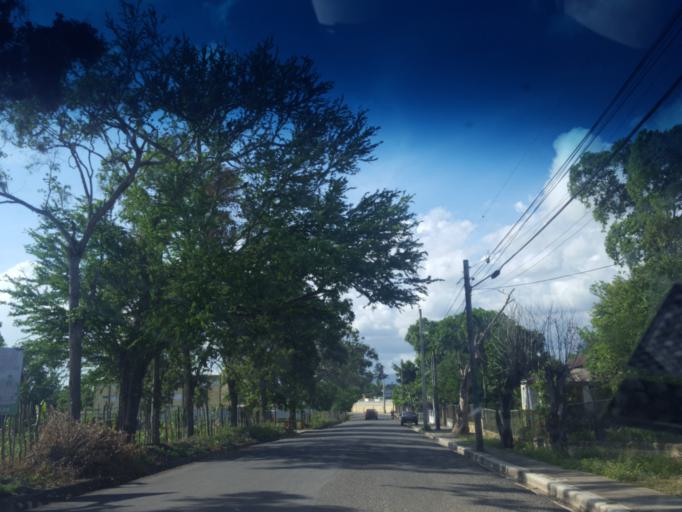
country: DO
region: La Vega
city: Rio Verde Arriba
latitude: 19.3651
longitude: -70.6051
